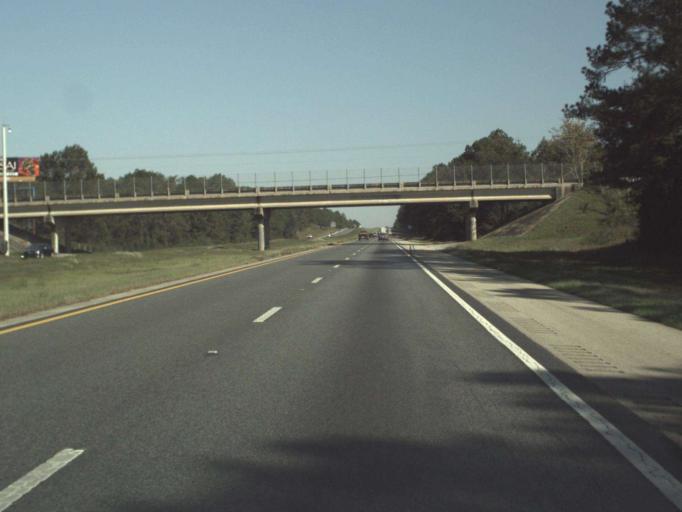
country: US
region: Florida
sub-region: Washington County
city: Chipley
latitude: 30.7465
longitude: -85.5388
